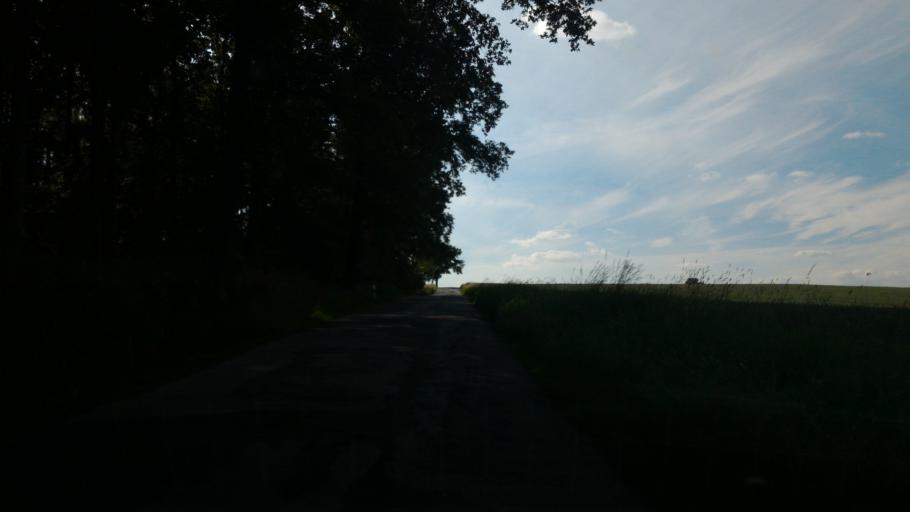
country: DE
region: Saxony
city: Olbersdorf
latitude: 50.8632
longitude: 14.7793
